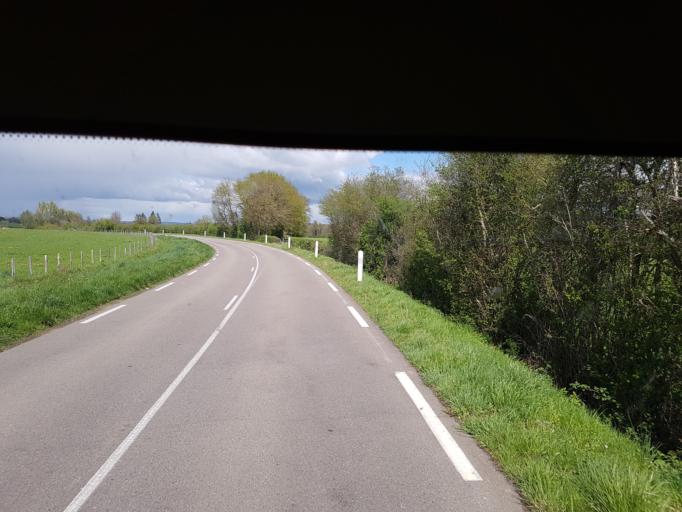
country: FR
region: Bourgogne
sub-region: Departement de Saone-et-Loire
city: Etang-sur-Arroux
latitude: 46.8852
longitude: 4.1873
